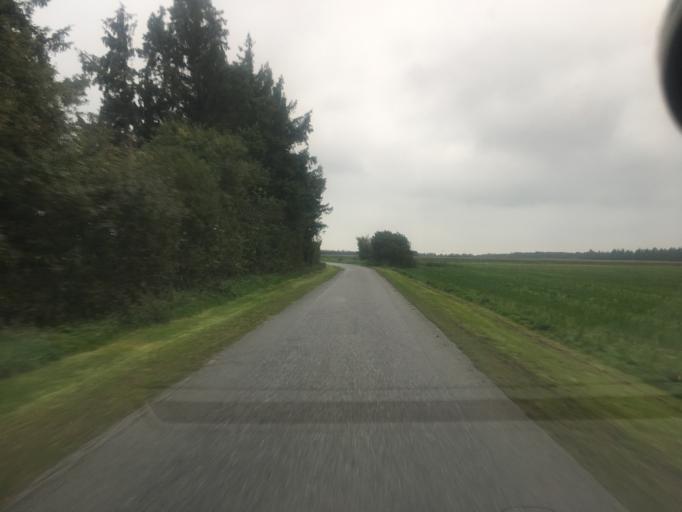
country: DK
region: South Denmark
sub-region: Tonder Kommune
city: Logumkloster
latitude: 54.9713
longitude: 8.9918
